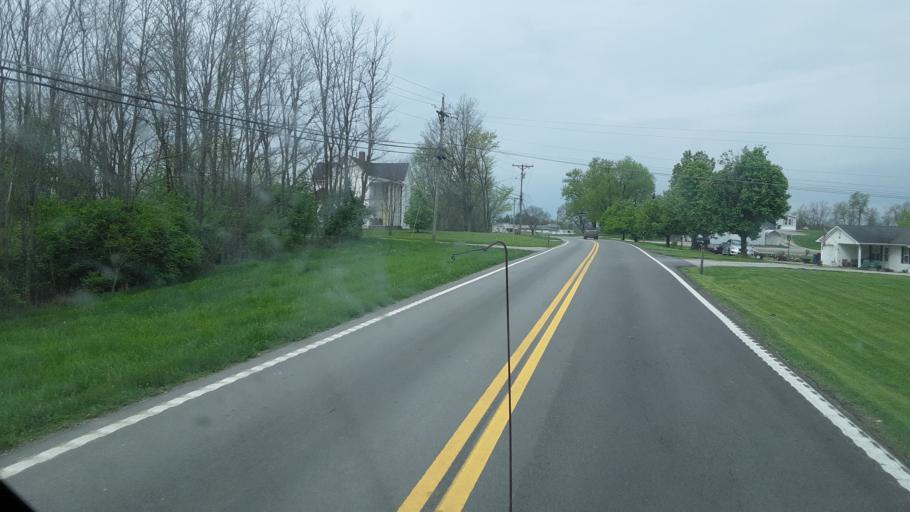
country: US
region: Kentucky
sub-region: Grant County
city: Dry Ridge
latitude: 38.6782
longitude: -84.6234
